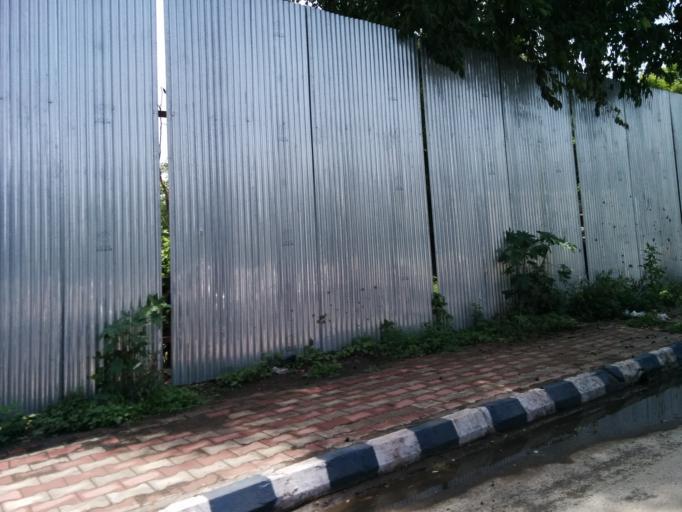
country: IN
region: Maharashtra
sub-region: Pune Division
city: Pune
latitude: 18.5339
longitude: 73.9145
